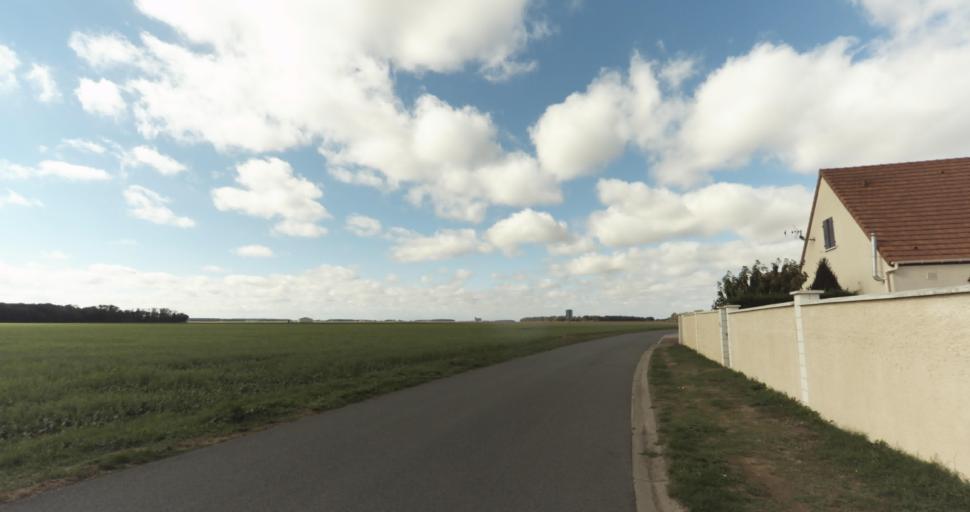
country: FR
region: Centre
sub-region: Departement d'Eure-et-Loir
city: Garnay
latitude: 48.7170
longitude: 1.3290
